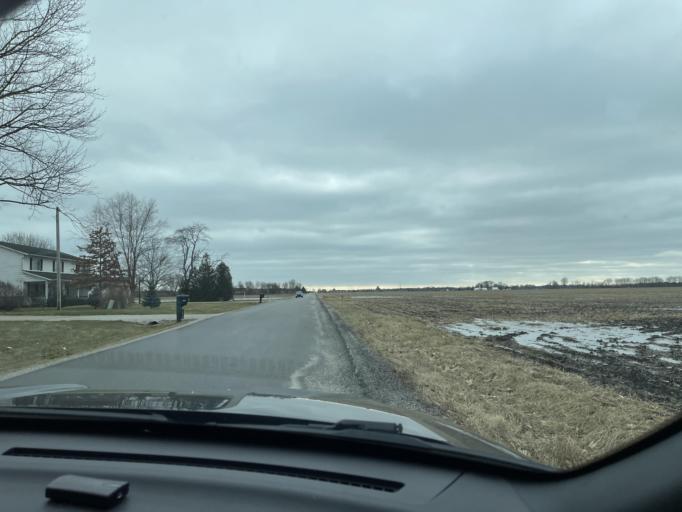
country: US
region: Illinois
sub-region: Sangamon County
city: Jerome
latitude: 39.7825
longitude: -89.7536
